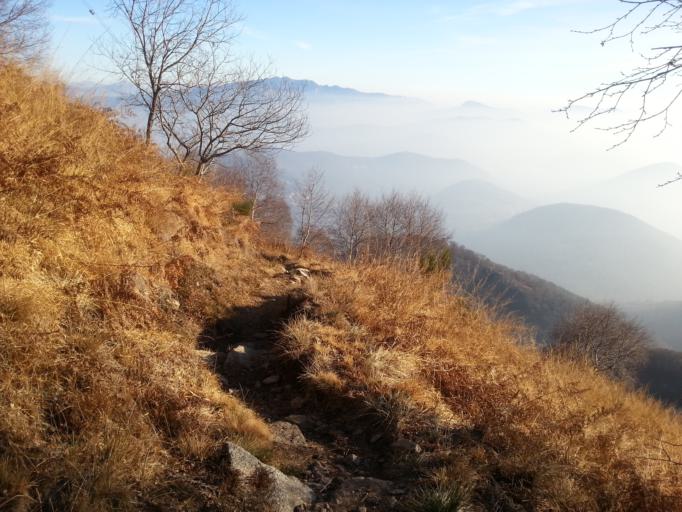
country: IT
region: Lombardy
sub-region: Provincia di Varese
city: Curiglia
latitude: 46.0378
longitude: 8.8377
